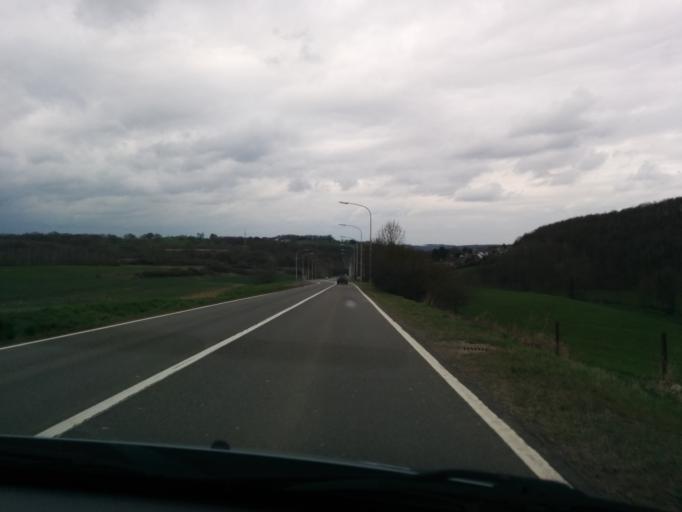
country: BE
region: Wallonia
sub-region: Province de Namur
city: Floreffe
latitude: 50.4149
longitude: 4.7470
